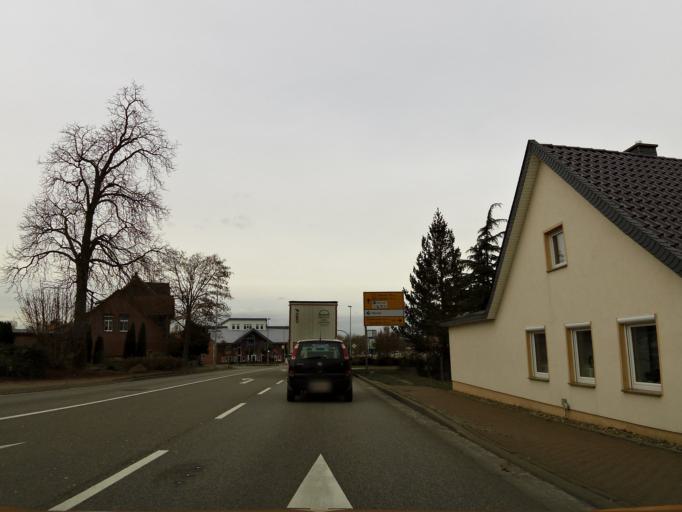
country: DE
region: Saxony-Anhalt
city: Salzwedel
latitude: 52.8416
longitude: 11.1705
